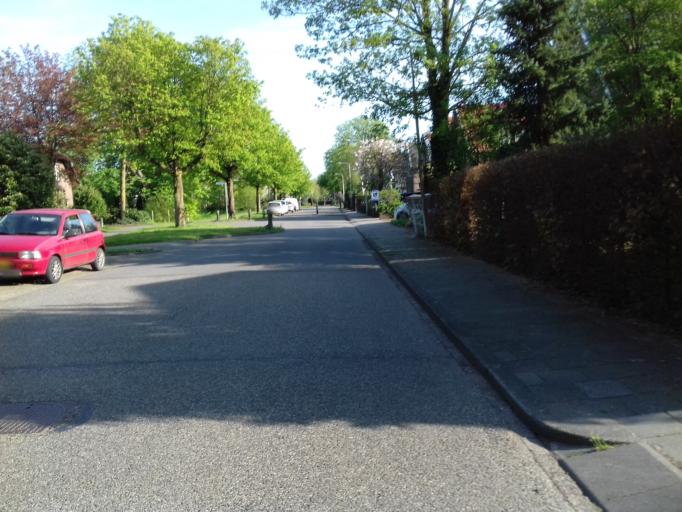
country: NL
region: Gelderland
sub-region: Gemeente Geldermalsen
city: Geldermalsen
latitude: 51.8835
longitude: 5.2773
